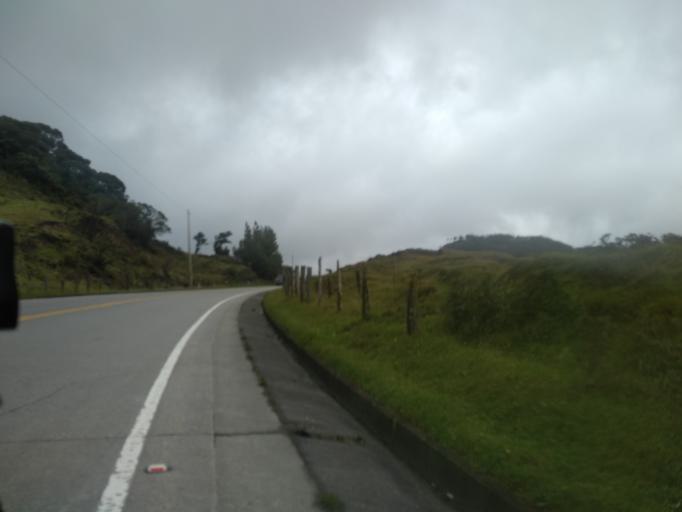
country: EC
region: Loja
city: Loja
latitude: -3.8843
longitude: -79.2634
